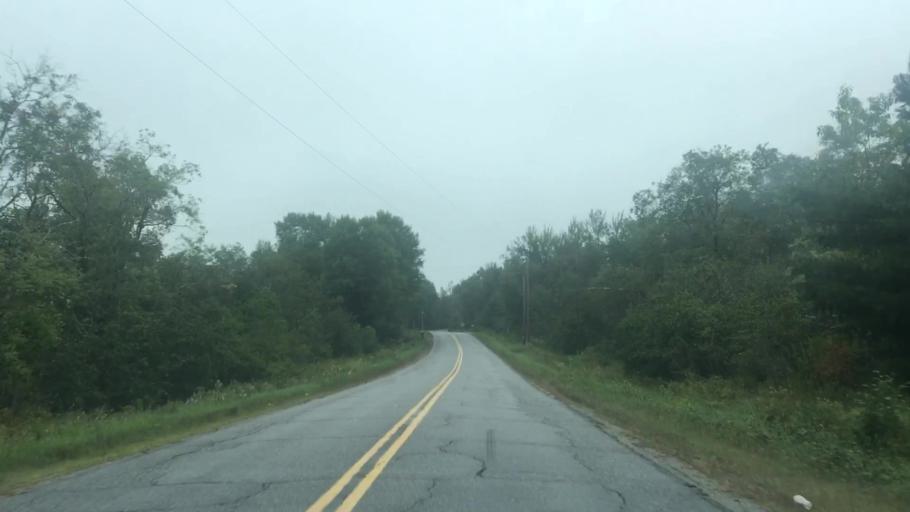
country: US
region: Maine
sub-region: Waldo County
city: Stockton Springs
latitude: 44.5477
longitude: -68.8742
